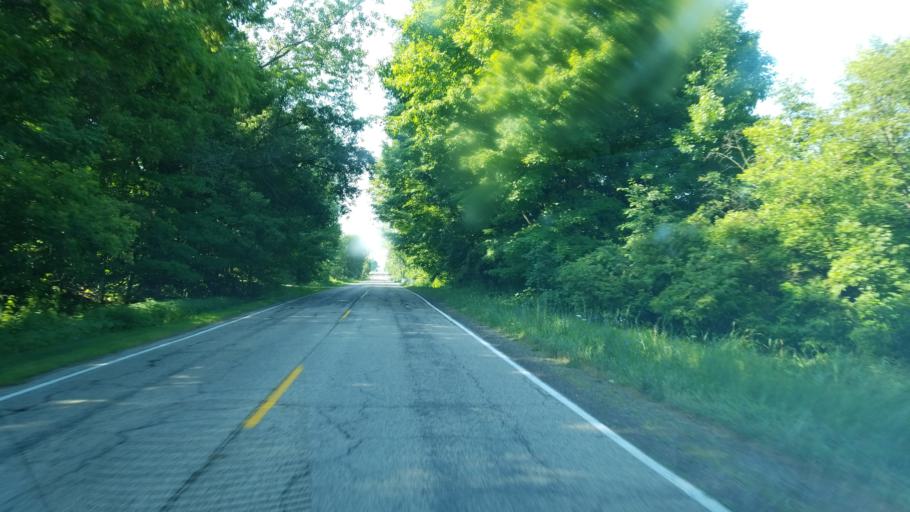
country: US
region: Michigan
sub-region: Kent County
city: Cedar Springs
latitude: 43.2901
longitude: -85.5518
